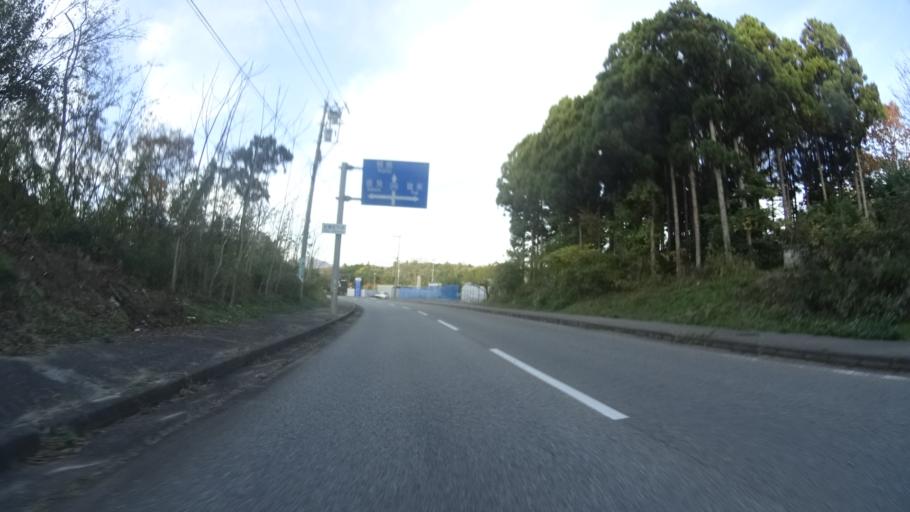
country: JP
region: Ishikawa
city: Nanao
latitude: 37.1529
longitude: 136.7206
